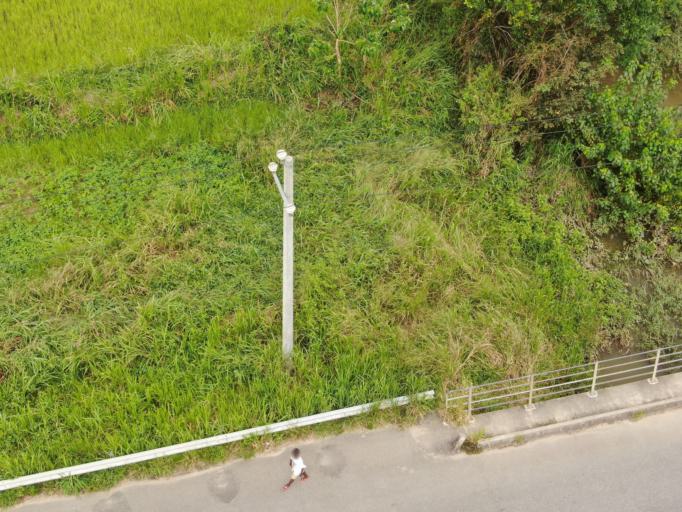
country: SL
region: Northern Province
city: Makali
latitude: 8.6280
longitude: -11.6588
